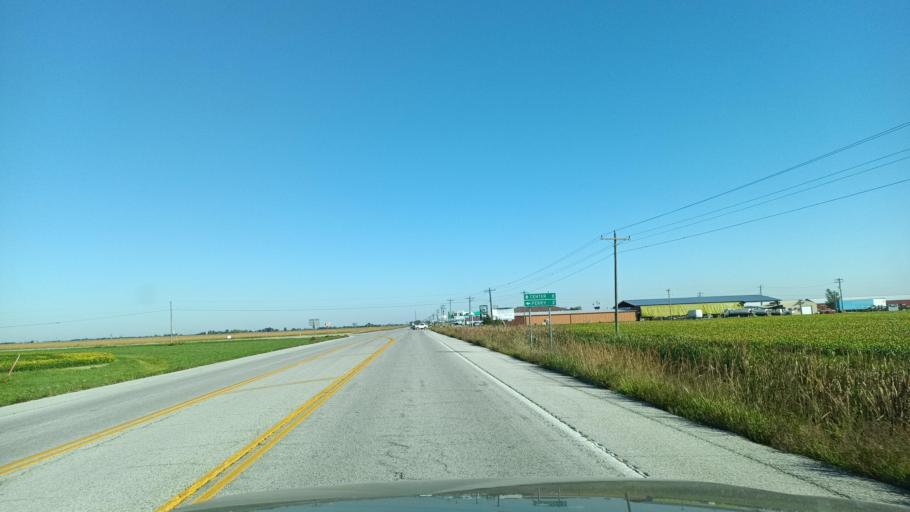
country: US
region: Missouri
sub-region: Audrain County
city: Vandalia
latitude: 39.4277
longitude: -91.6364
